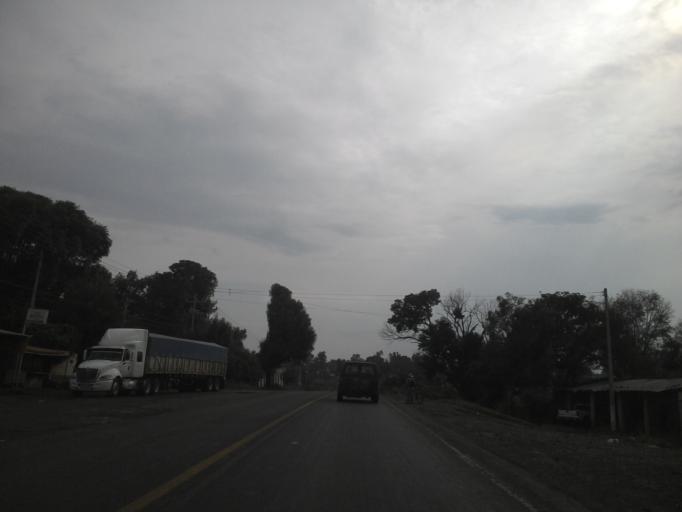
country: MX
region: Jalisco
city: Tepatitlan de Morelos
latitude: 20.7722
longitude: -102.8003
